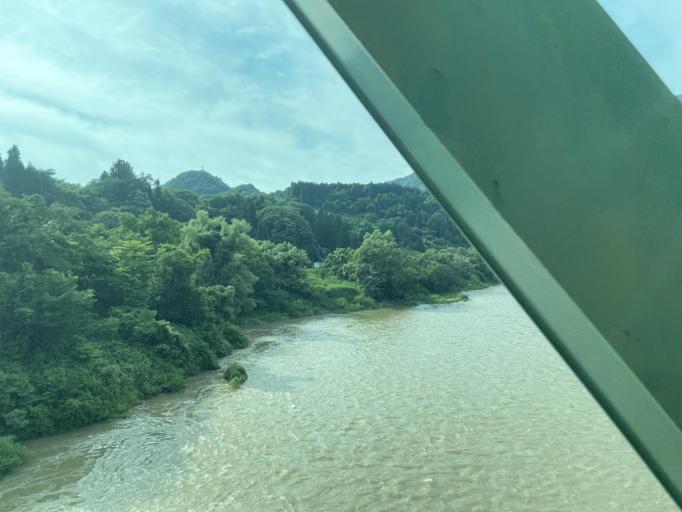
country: JP
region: Niigata
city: Shibata
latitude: 37.6996
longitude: 139.4902
